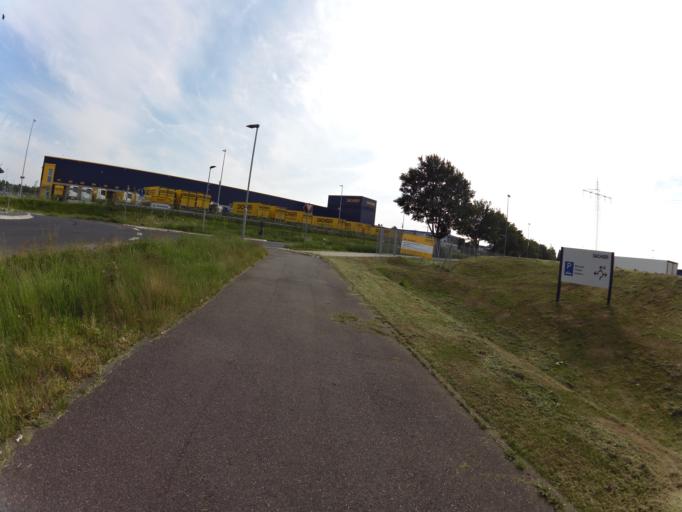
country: DE
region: North Rhine-Westphalia
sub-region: Regierungsbezirk Koln
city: Alsdorf
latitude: 50.8762
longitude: 6.1921
